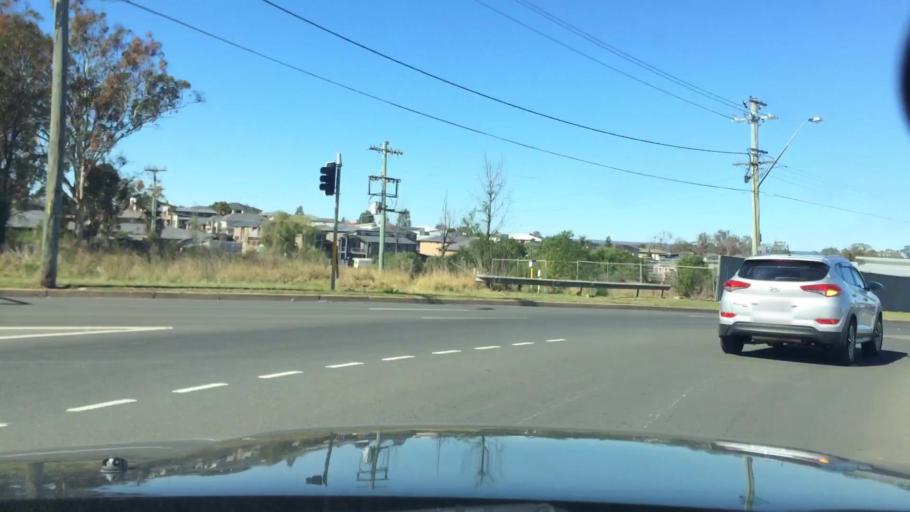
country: AU
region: New South Wales
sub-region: Campbelltown Municipality
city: Glenfield
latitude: -33.9580
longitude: 150.8871
